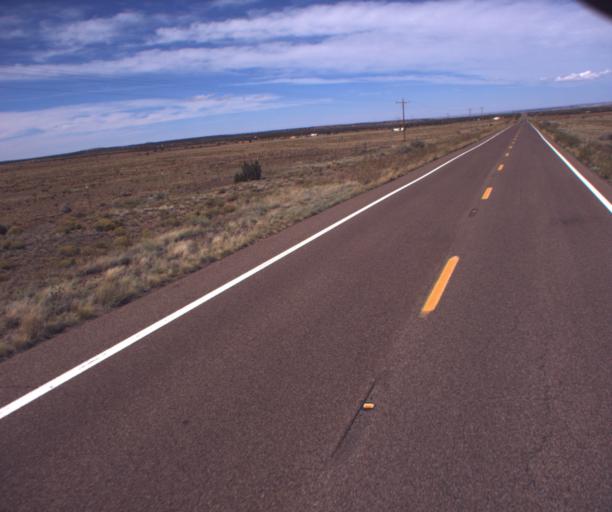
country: US
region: Arizona
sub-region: Apache County
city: Saint Johns
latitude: 34.5031
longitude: -109.6212
